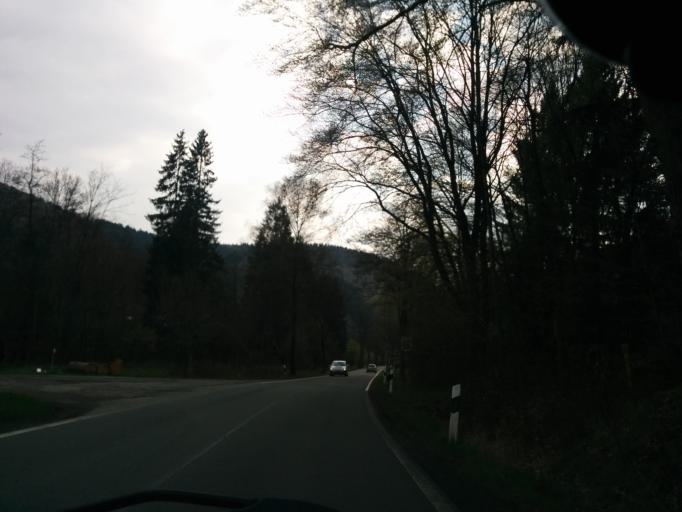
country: DE
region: Lower Saxony
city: Bad Lauterberg im Harz
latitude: 51.6630
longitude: 10.5061
